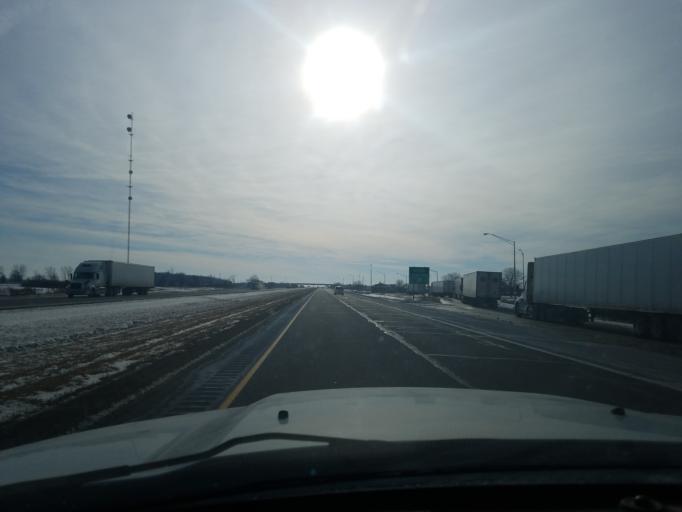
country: US
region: Indiana
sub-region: Huntington County
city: Warren
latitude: 40.7485
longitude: -85.4070
